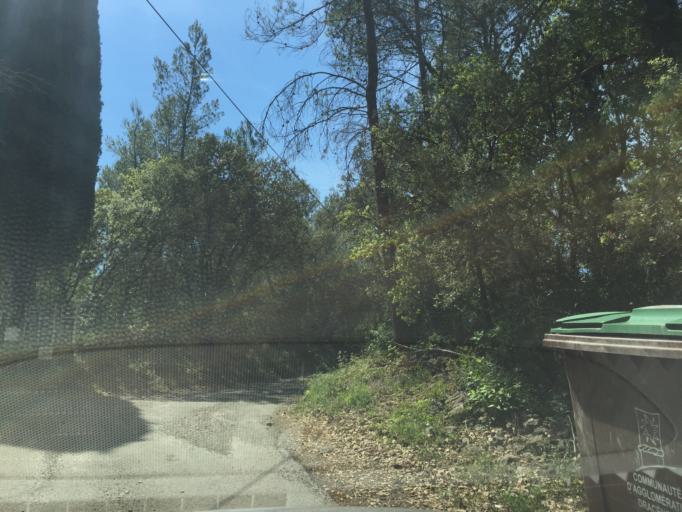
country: FR
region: Provence-Alpes-Cote d'Azur
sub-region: Departement du Var
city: Lorgues
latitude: 43.4745
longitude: 6.3691
